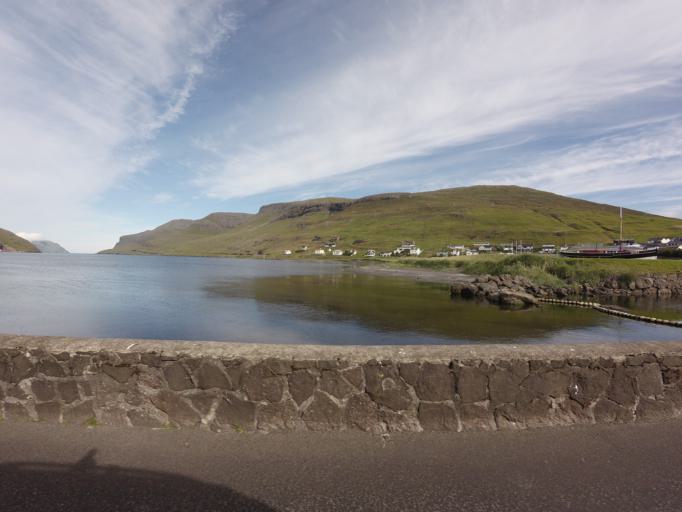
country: FO
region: Vagar
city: Sorvagur
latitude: 62.0707
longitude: -7.3118
